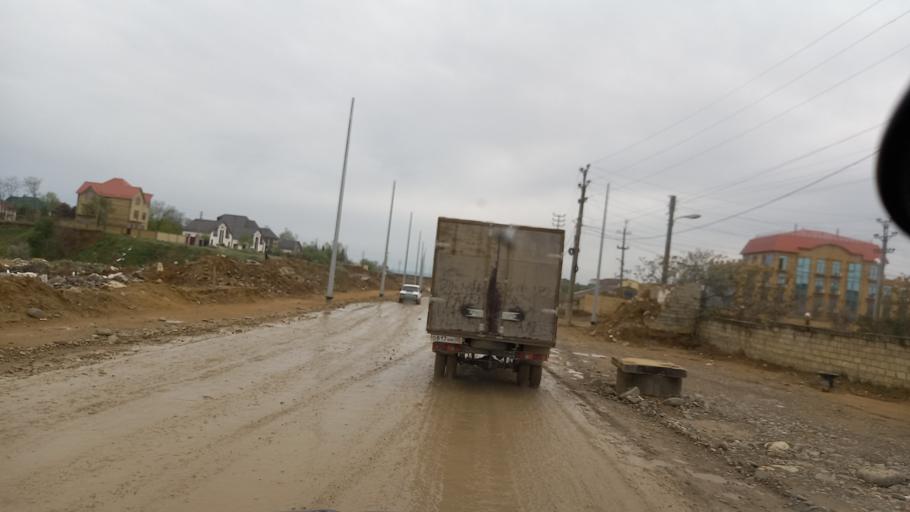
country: RU
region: Dagestan
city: Derbent
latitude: 42.0990
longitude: 48.2859
